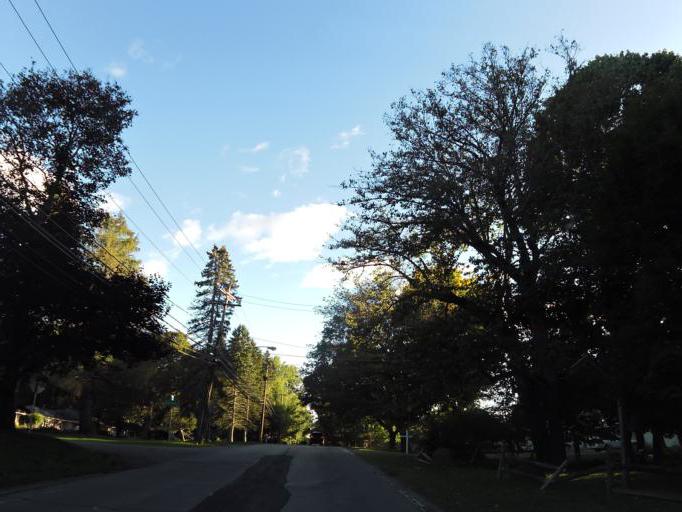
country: US
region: New York
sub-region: Erie County
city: Billington Heights
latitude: 42.7806
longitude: -78.6208
